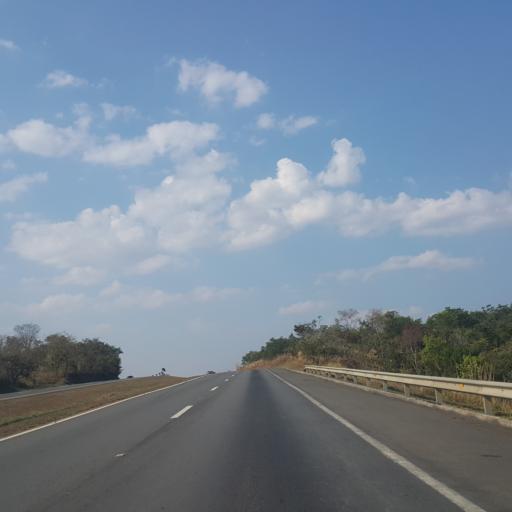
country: BR
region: Goias
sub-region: Abadiania
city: Abadiania
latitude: -16.1674
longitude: -48.6360
